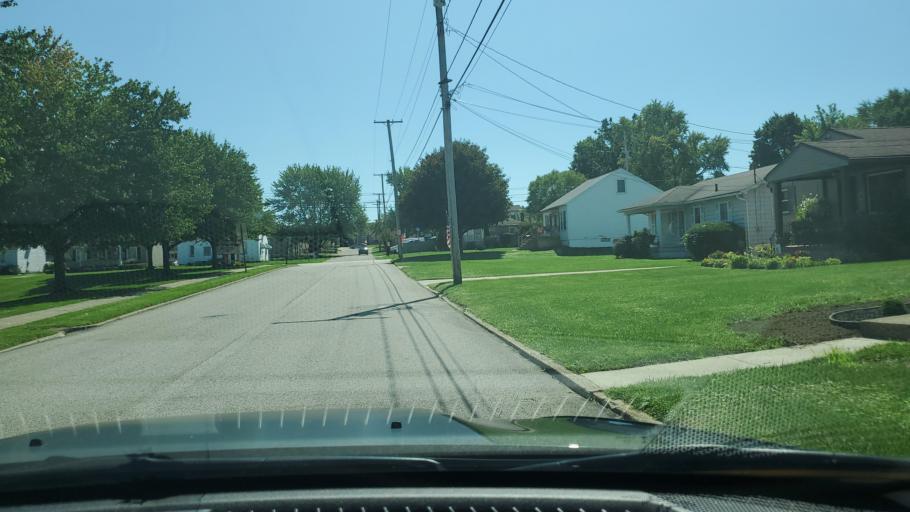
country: US
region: Ohio
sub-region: Mahoning County
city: Struthers
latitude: 41.0566
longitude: -80.6101
